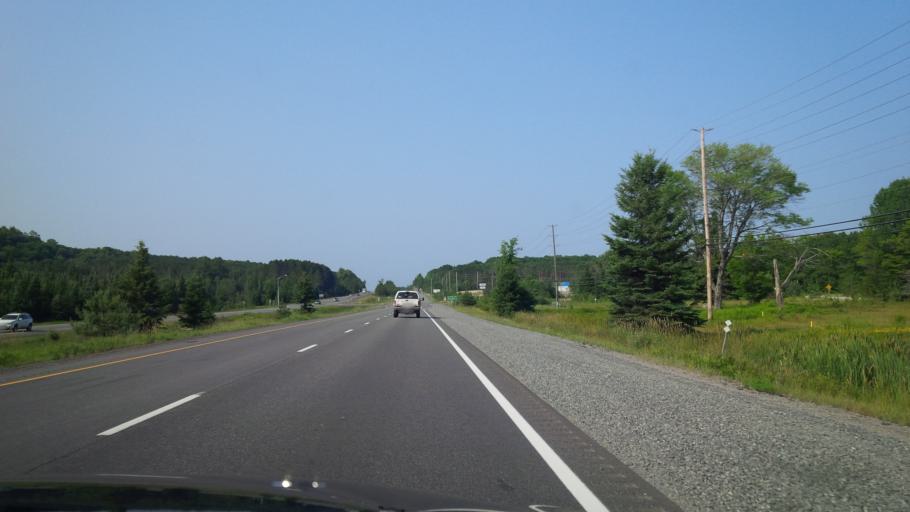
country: CA
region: Ontario
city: Huntsville
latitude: 45.2939
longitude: -79.2642
